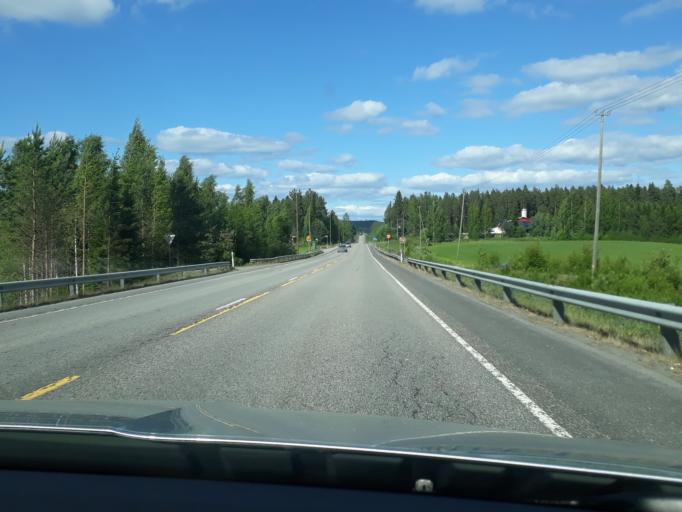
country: FI
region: Central Finland
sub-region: AEaenekoski
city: AEaenekoski
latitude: 62.6536
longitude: 25.7217
